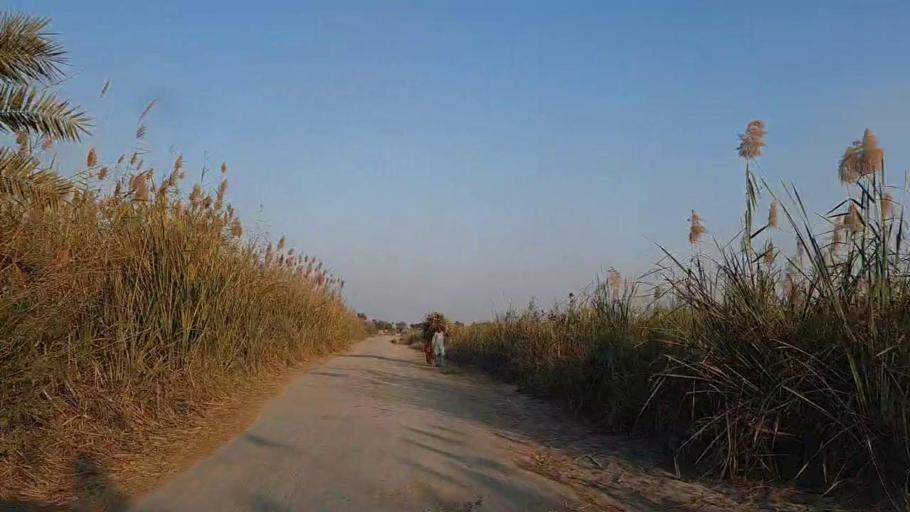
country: PK
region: Sindh
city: Daur
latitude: 26.5105
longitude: 68.3029
